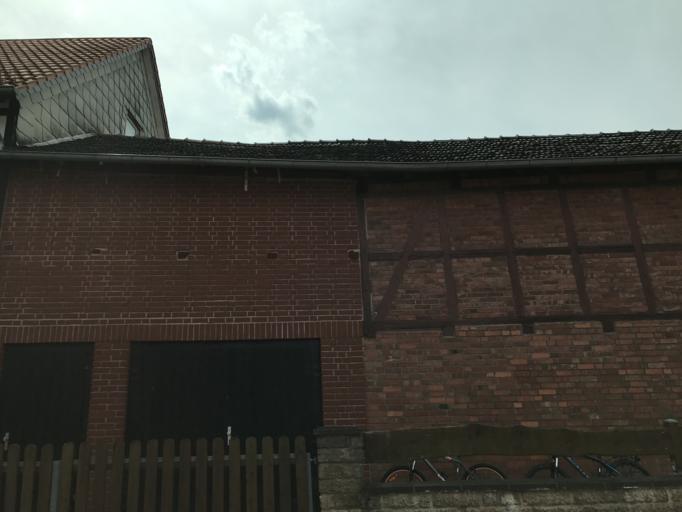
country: DE
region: Thuringia
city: Weissenborn-Luderode
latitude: 51.5540
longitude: 10.3762
